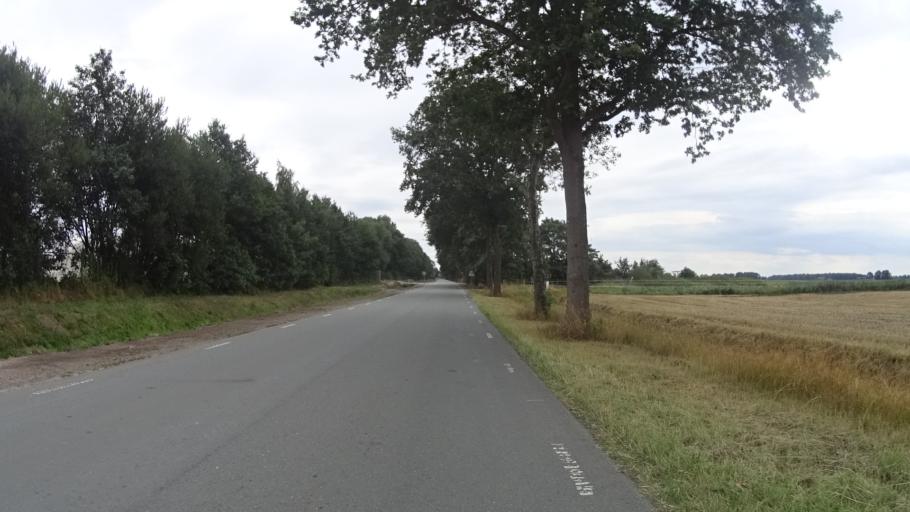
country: NL
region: Groningen
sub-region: Gemeente Slochteren
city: Slochteren
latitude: 53.1863
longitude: 6.8505
